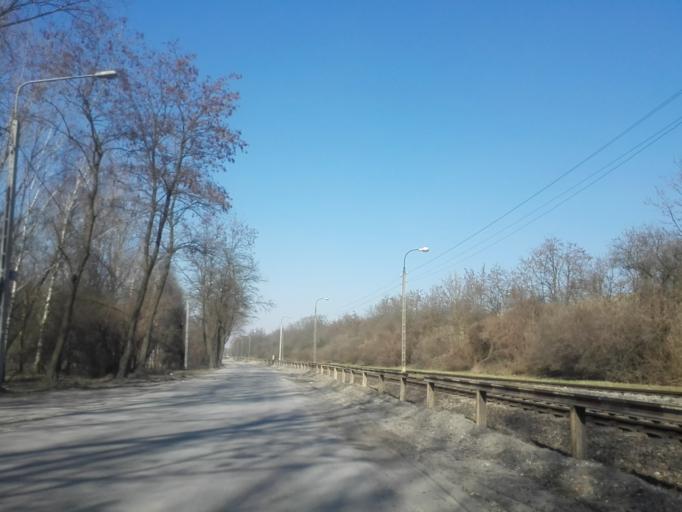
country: PL
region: Masovian Voivodeship
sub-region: Warszawa
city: Wilanow
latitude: 52.1473
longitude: 21.1438
